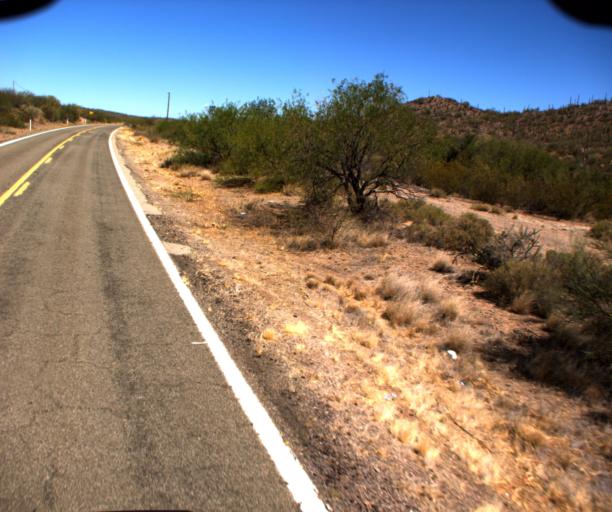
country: US
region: Arizona
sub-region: Pima County
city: Sells
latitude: 32.1715
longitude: -112.1511
